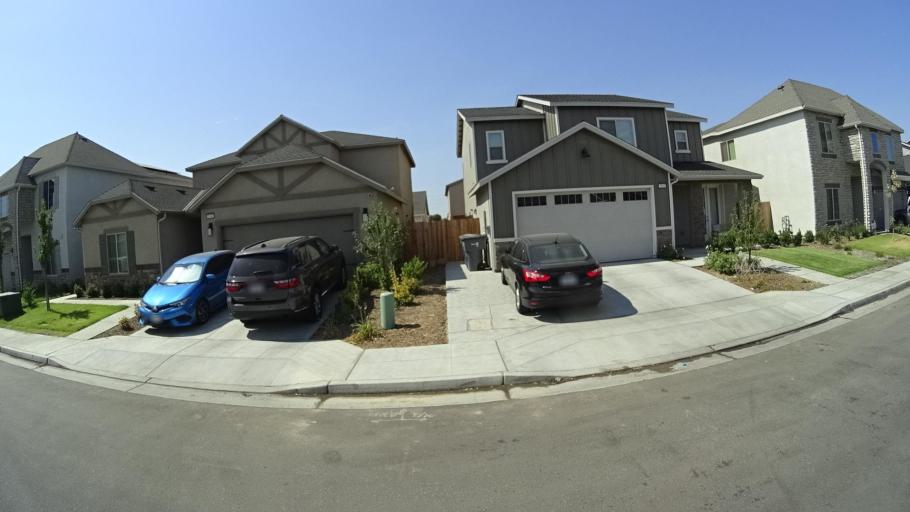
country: US
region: California
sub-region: Fresno County
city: Sunnyside
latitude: 36.7175
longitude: -119.6846
